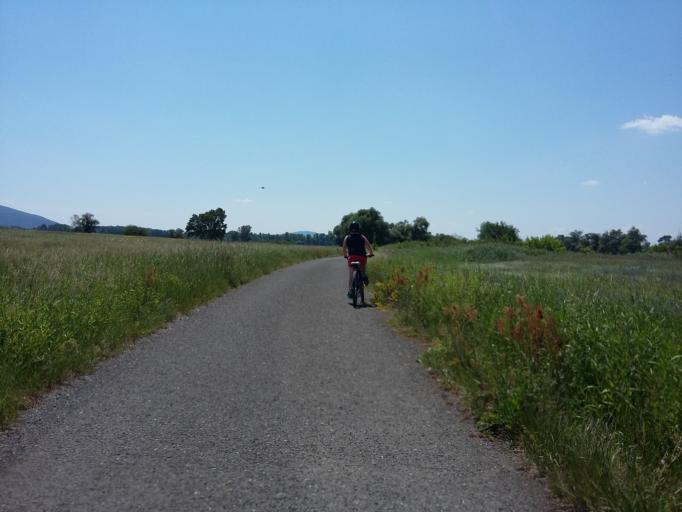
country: AT
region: Lower Austria
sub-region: Politischer Bezirk Ganserndorf
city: Marchegg
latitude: 48.2543
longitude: 16.9535
